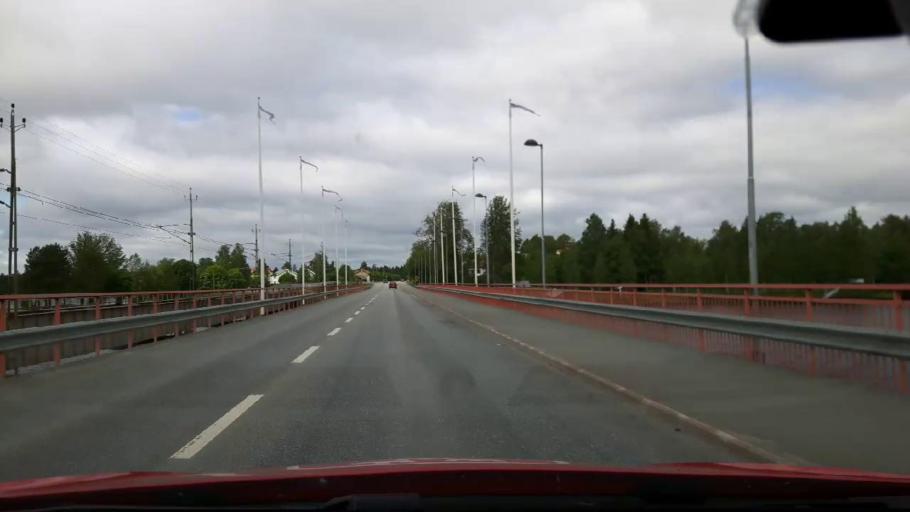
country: SE
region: Jaemtland
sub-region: Krokoms Kommun
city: Krokom
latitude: 63.3226
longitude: 14.4537
